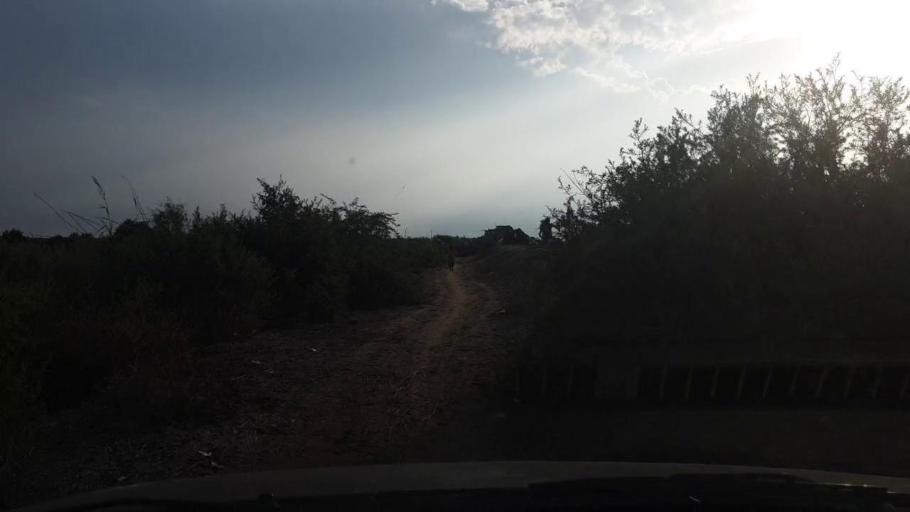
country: PK
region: Sindh
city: Badin
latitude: 24.4288
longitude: 68.6675
